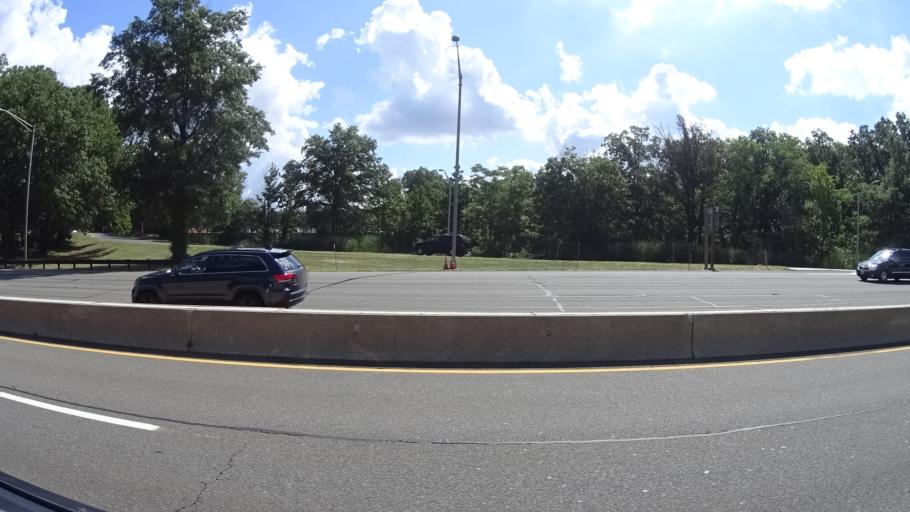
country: US
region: New Jersey
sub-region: Union County
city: Kenilworth
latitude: 40.6790
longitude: -74.2785
